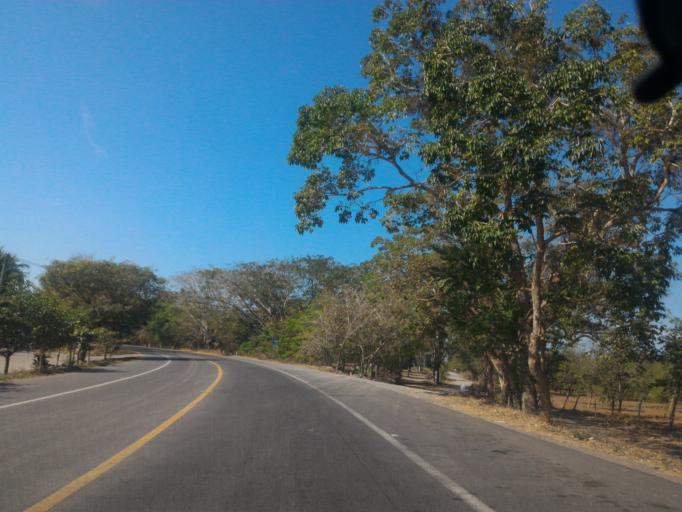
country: MX
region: Colima
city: Tecoman
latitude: 18.9012
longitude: -103.9131
